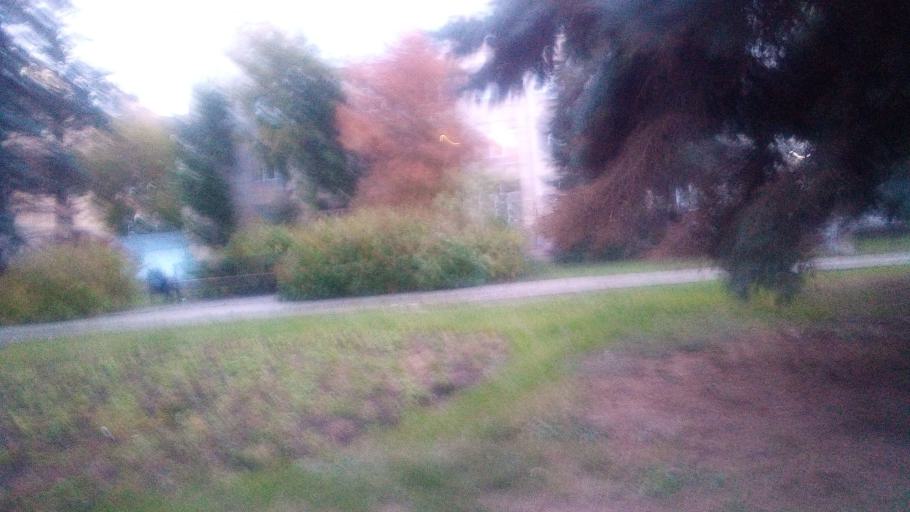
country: RU
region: Chelyabinsk
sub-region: Gorod Chelyabinsk
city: Chelyabinsk
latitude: 55.1588
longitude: 61.3702
